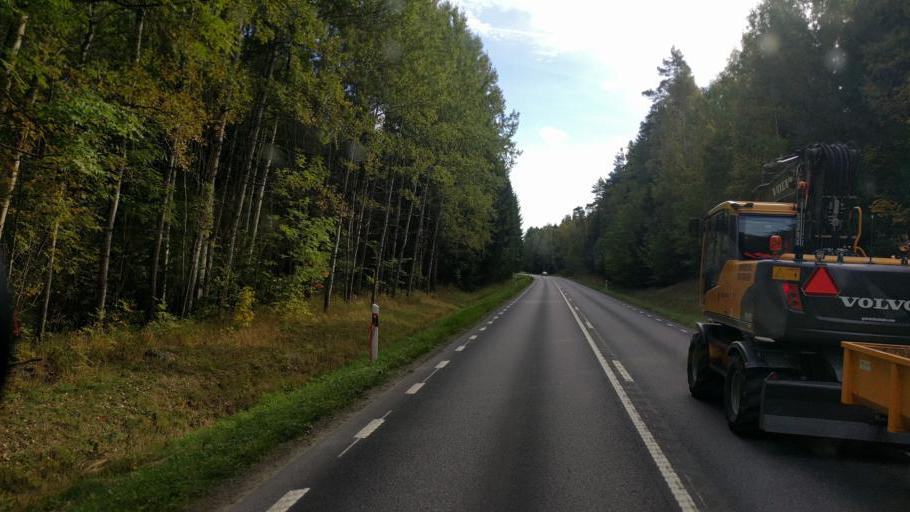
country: SE
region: OEstergoetland
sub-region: Kinda Kommun
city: Kisa
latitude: 57.9676
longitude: 15.6540
